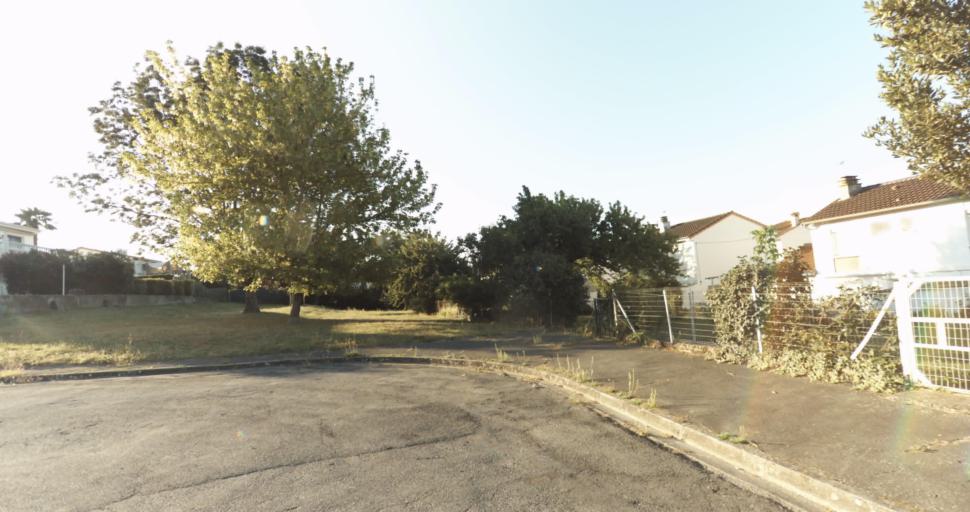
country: FR
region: Midi-Pyrenees
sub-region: Departement de la Haute-Garonne
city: L'Union
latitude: 43.6604
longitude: 1.4742
